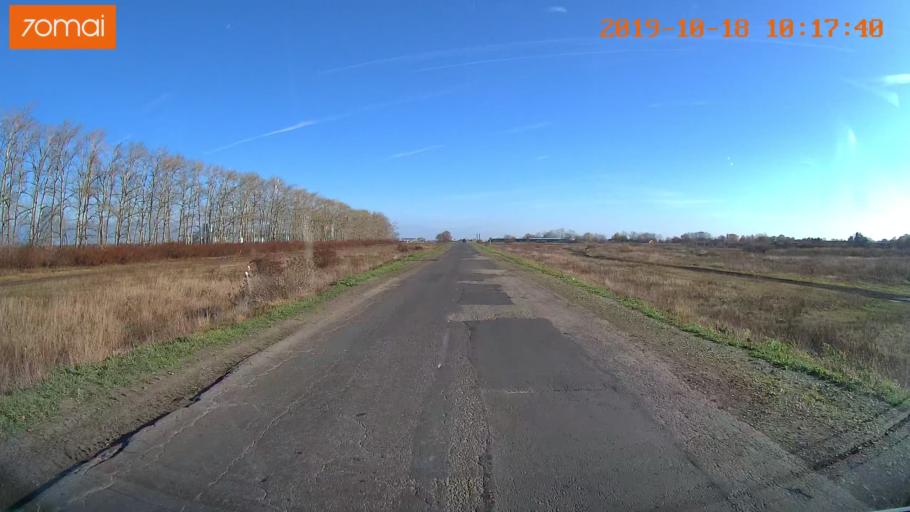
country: RU
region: Tula
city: Kurkino
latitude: 53.4133
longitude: 38.6228
